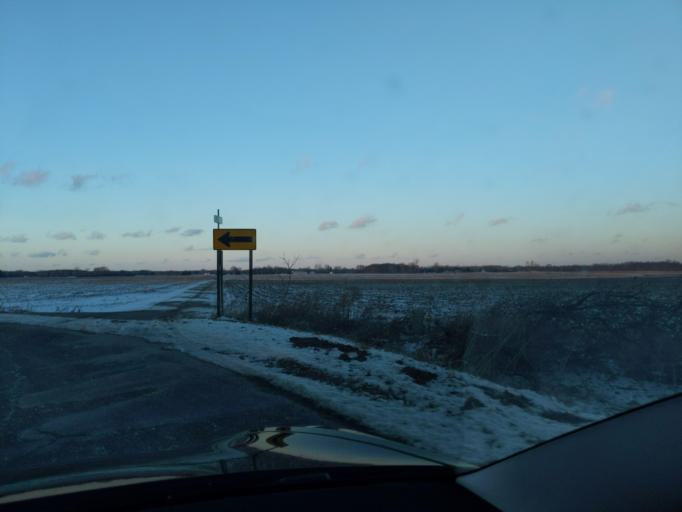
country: US
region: Michigan
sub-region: Ingham County
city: Stockbridge
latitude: 42.4679
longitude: -84.2779
